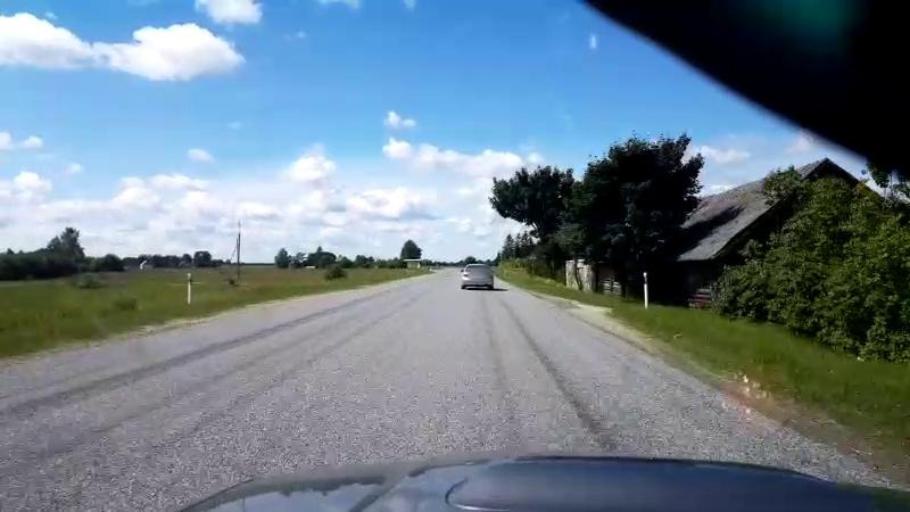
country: EE
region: Laeaene-Virumaa
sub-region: Tapa vald
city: Tapa
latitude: 59.2227
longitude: 25.8943
